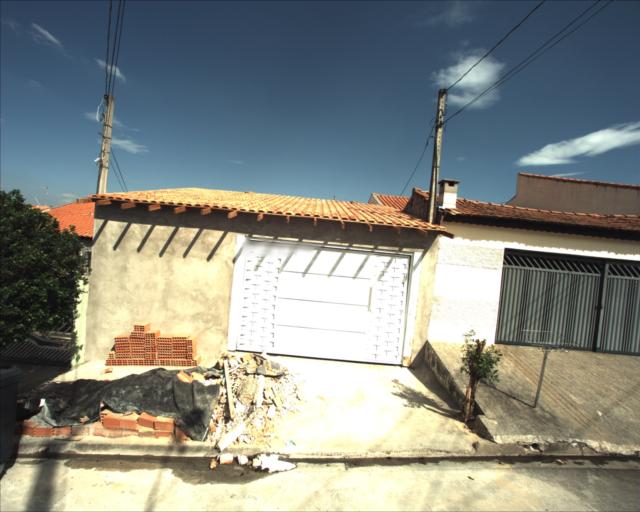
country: BR
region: Sao Paulo
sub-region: Sorocaba
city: Sorocaba
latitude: -23.4811
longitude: -47.5088
